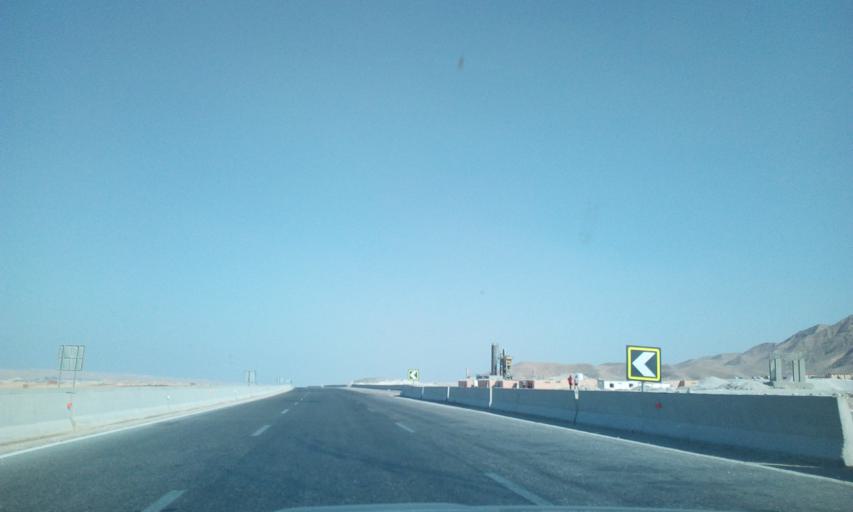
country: EG
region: As Suways
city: Ain Sukhna
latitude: 29.4458
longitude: 32.3506
